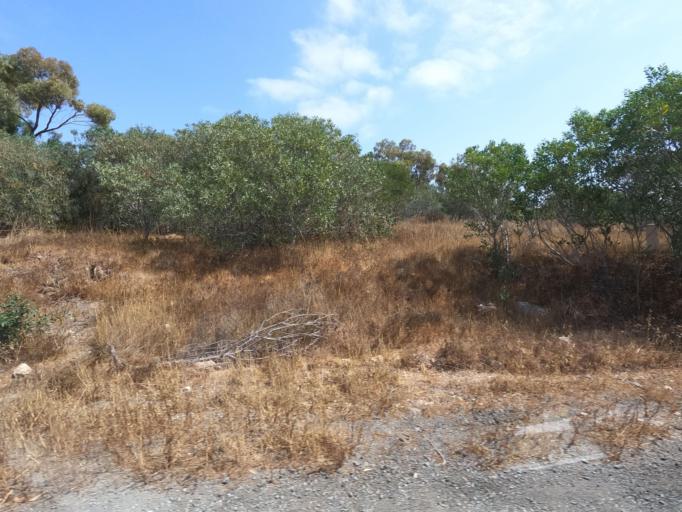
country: CY
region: Ammochostos
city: Protaras
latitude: 35.0048
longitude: 34.0507
